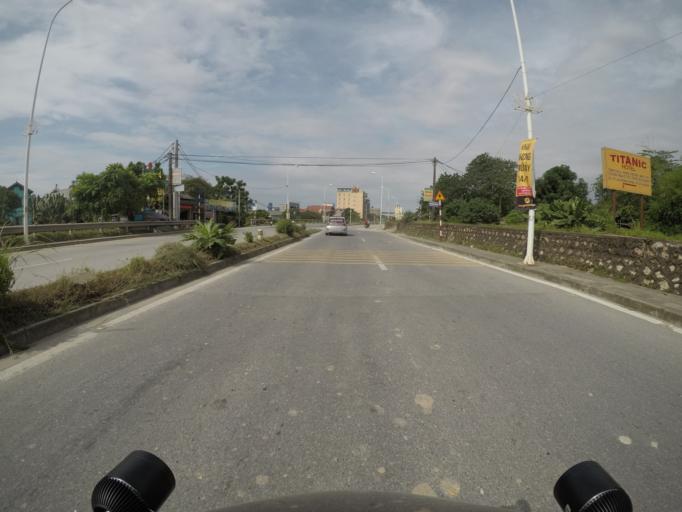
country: VN
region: Ha Noi
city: Tay Ho
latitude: 21.0902
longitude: 105.7919
